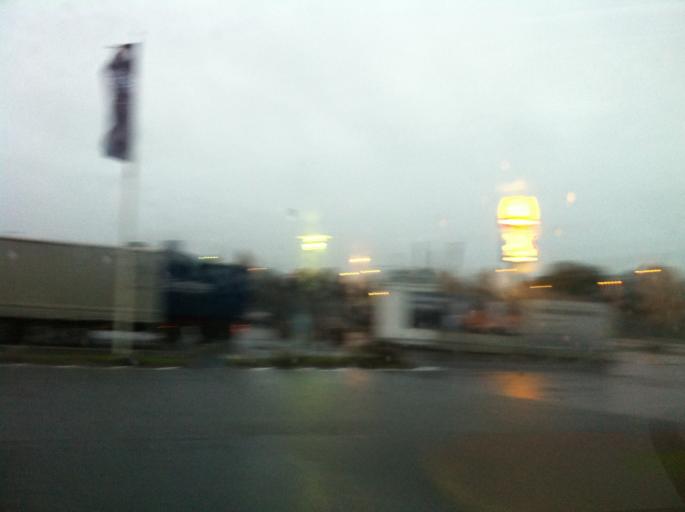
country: SE
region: Joenkoeping
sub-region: Varnamo Kommun
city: Varnamo
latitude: 57.1635
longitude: 14.0733
